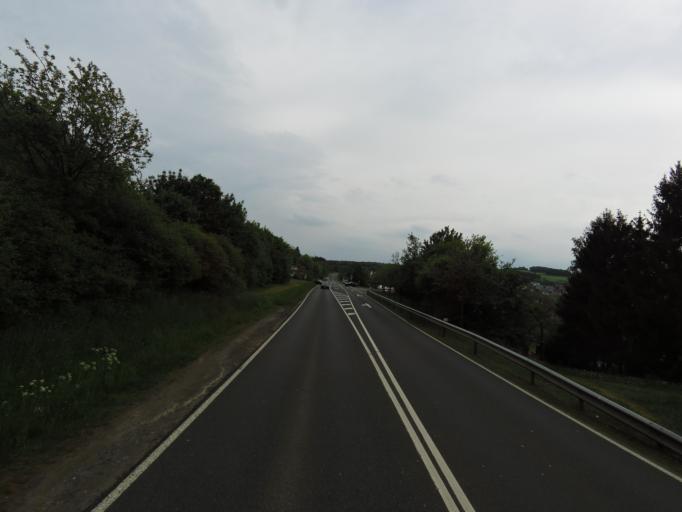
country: DE
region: Rheinland-Pfalz
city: Waldesch
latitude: 50.2836
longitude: 7.5480
